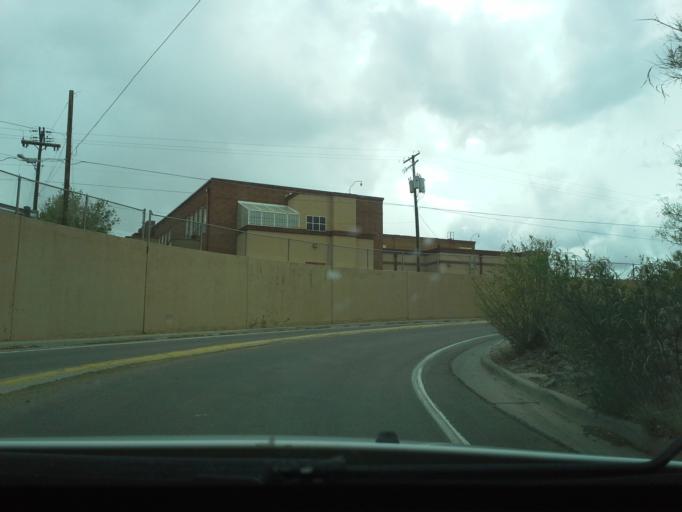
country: US
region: New Mexico
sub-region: Hidalgo County
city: Lordsburg
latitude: 32.3501
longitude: -108.7100
